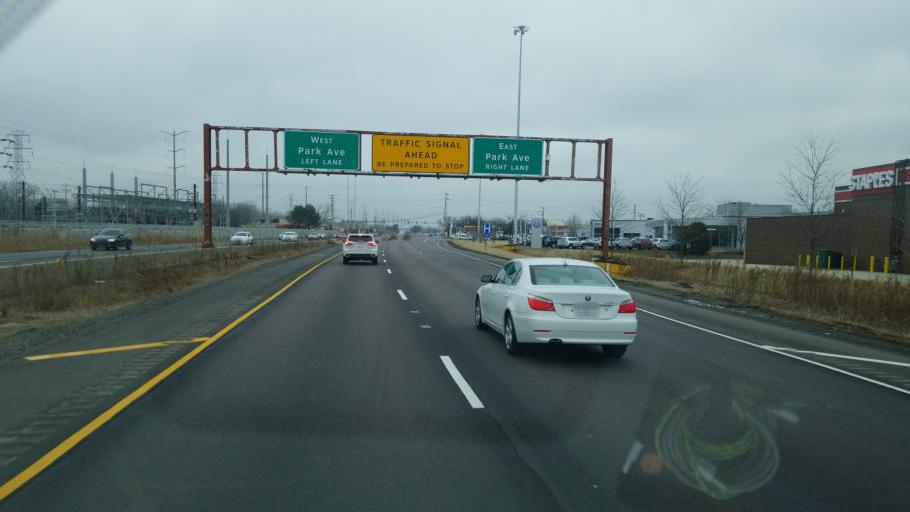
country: US
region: Illinois
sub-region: Lake County
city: Highwood
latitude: 42.1868
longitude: -87.8237
